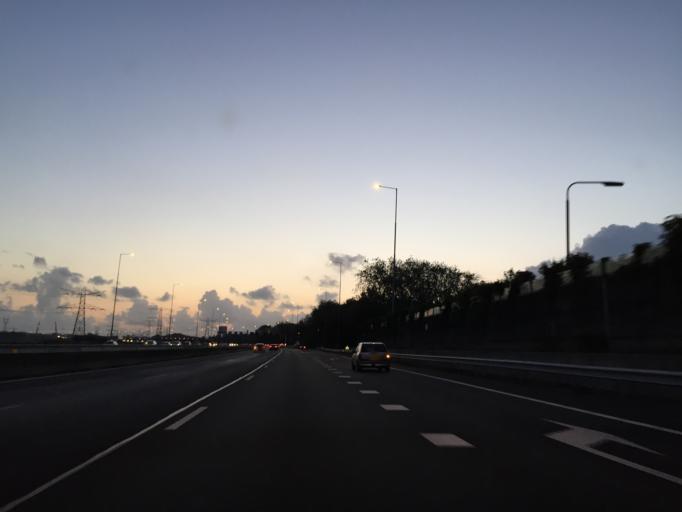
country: NL
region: North Holland
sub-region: Gemeente Weesp
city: Weesp
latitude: 52.3296
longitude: 5.0559
